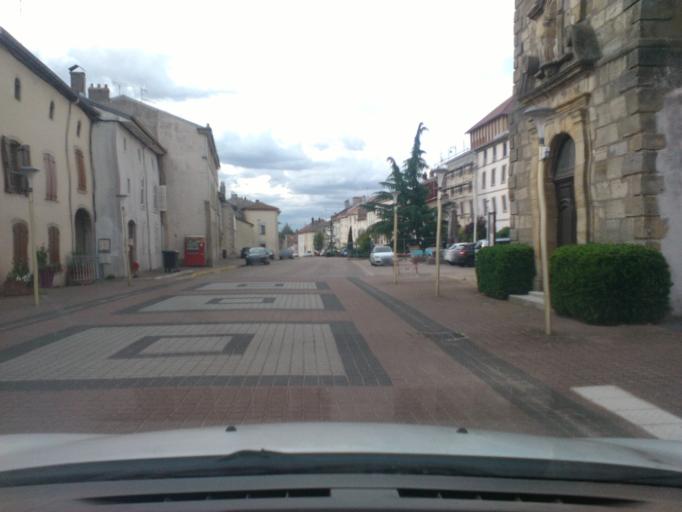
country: FR
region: Lorraine
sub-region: Departement des Vosges
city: Portieux
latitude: 48.3442
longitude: 6.3442
